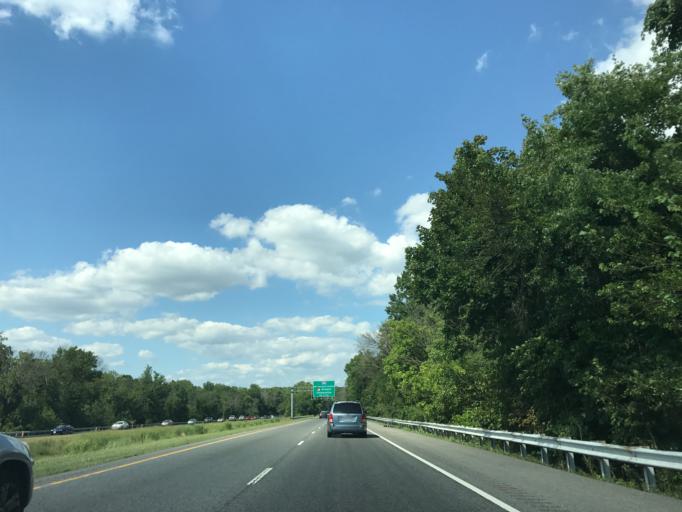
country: US
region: Maryland
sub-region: Howard County
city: Hanover
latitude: 39.1876
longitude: -76.7152
